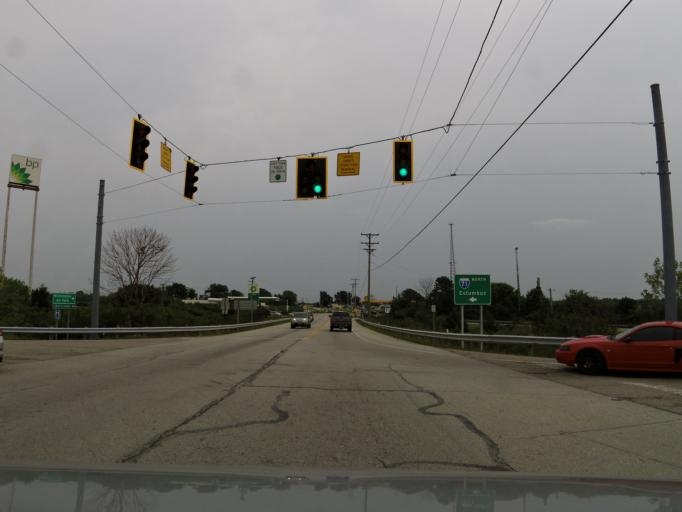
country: US
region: Ohio
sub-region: Clinton County
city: Wilmington
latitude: 39.4853
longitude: -83.9401
